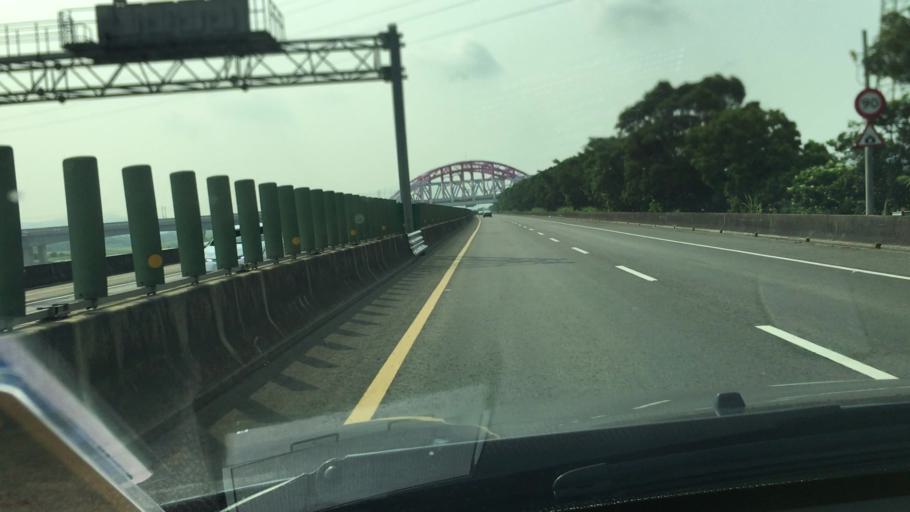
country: TW
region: Taiwan
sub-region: Hsinchu
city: Zhubei
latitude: 24.7967
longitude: 121.0316
